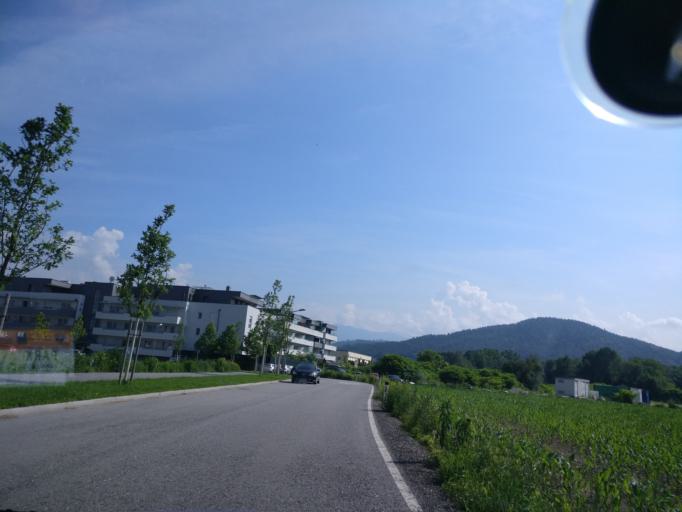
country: AT
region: Carinthia
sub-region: Klagenfurt am Woerthersee
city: Klagenfurt am Woerthersee
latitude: 46.6149
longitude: 14.2681
